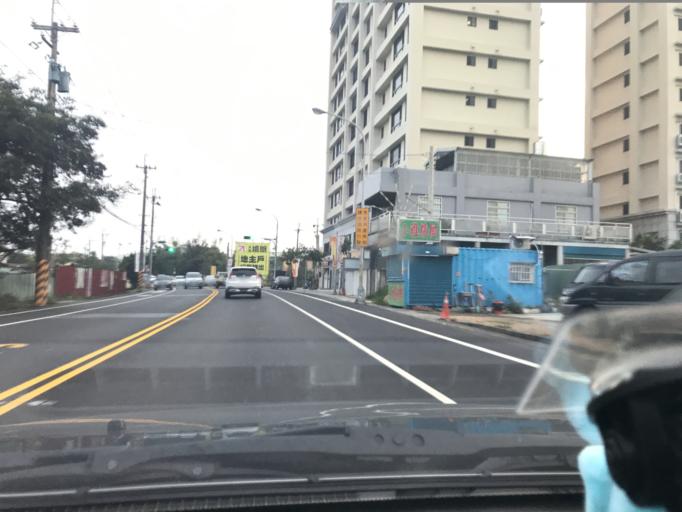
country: TW
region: Taiwan
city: Daxi
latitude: 24.8759
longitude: 121.2183
